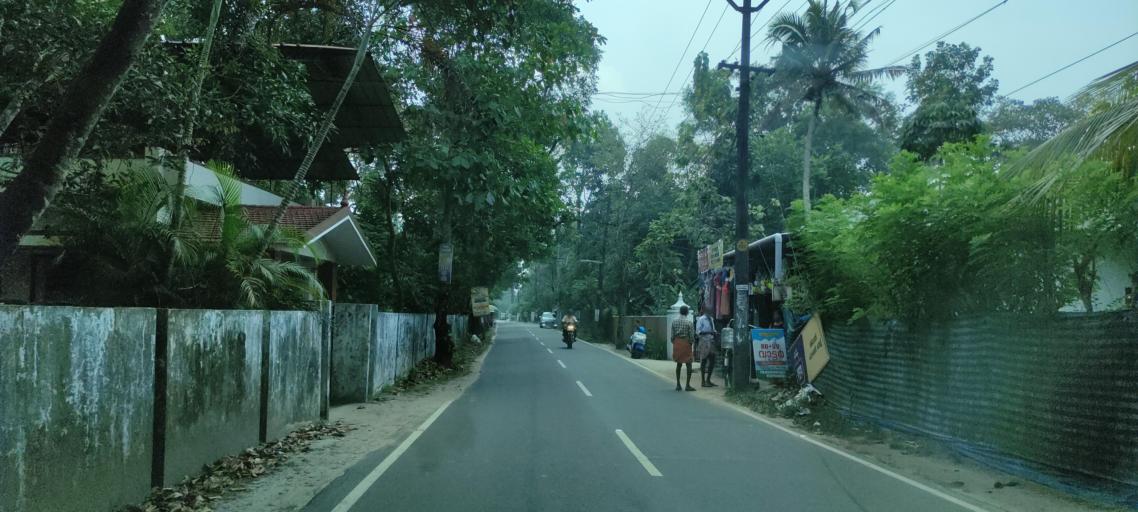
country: IN
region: Kerala
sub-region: Alappuzha
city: Alleppey
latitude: 9.5693
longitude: 76.3355
